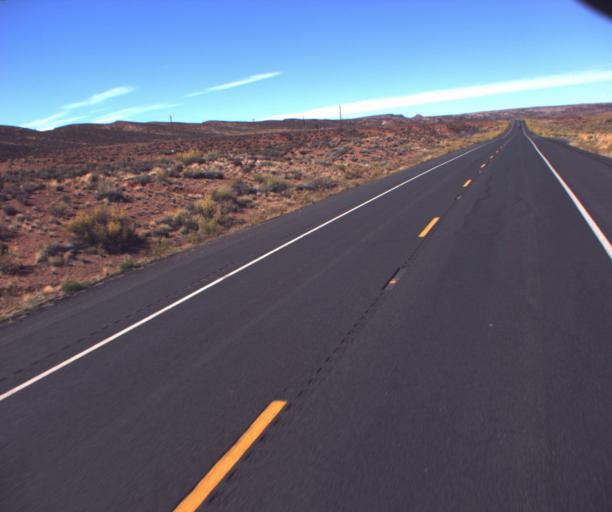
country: US
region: Arizona
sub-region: Coconino County
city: Tuba City
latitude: 36.3079
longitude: -111.4649
